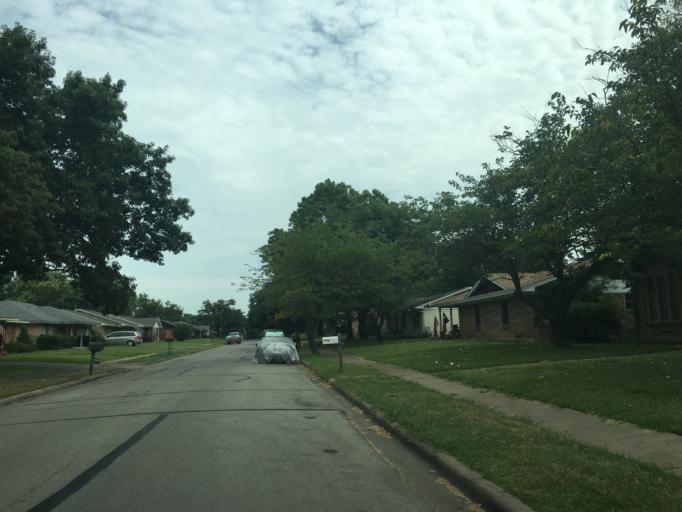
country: US
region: Texas
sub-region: Collin County
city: Wylie
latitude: 33.0065
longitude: -96.5329
